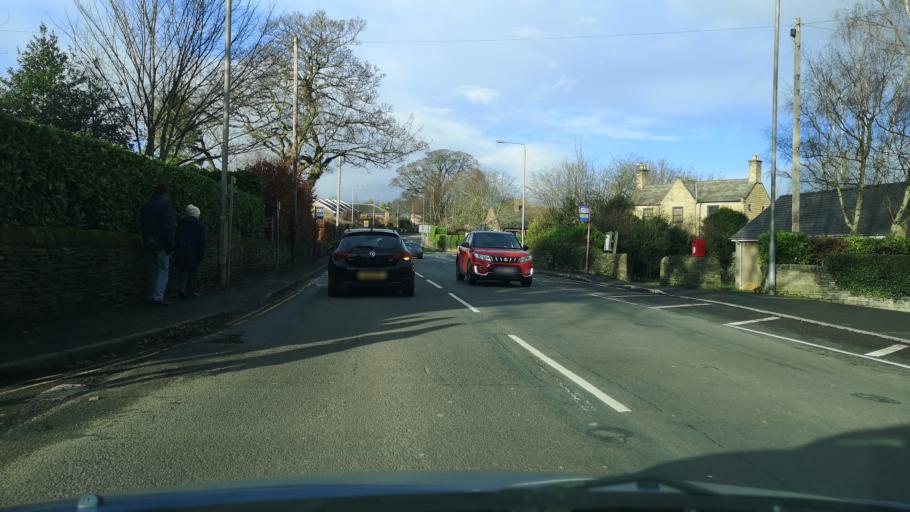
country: GB
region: England
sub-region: City and Borough of Wakefield
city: Horbury
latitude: 53.6181
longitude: -1.5670
